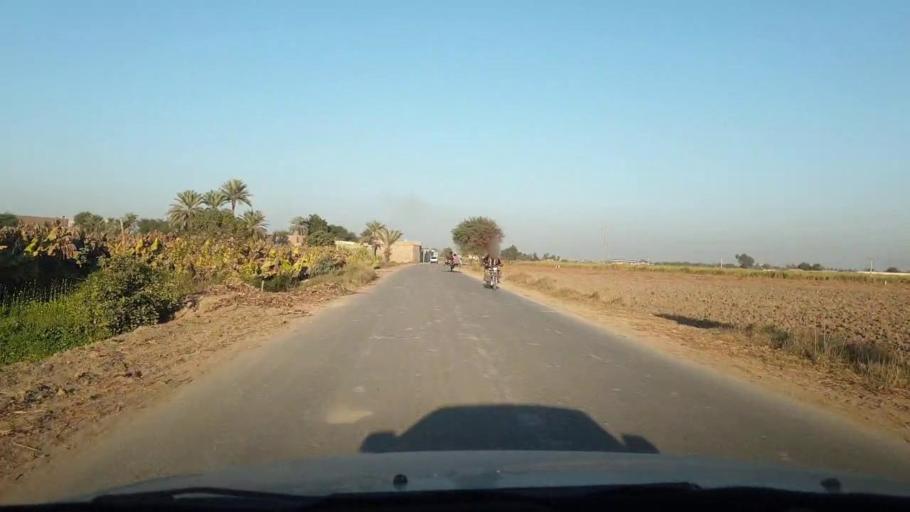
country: PK
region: Sindh
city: Ghotki
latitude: 27.9958
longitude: 69.2766
